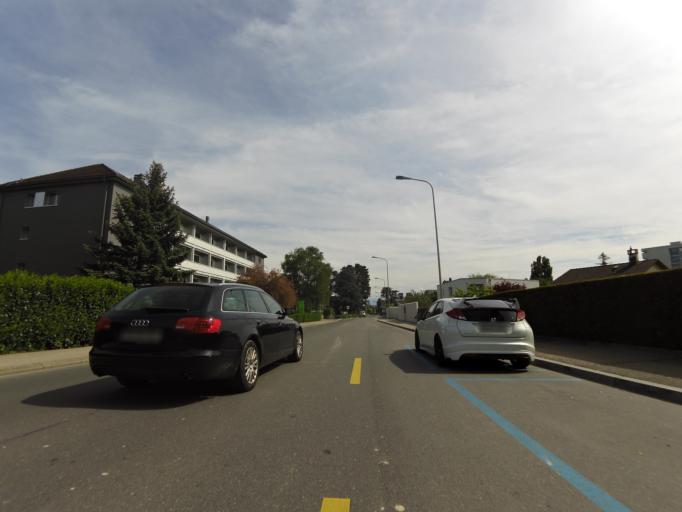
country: CH
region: Vaud
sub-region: Nyon District
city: Nyon
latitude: 46.3930
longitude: 6.2310
